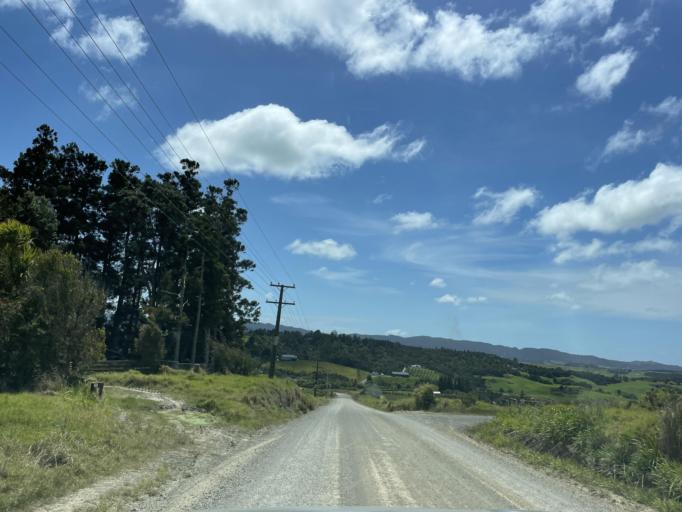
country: NZ
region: Auckland
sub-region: Auckland
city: Wellsford
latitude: -36.1445
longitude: 174.5406
